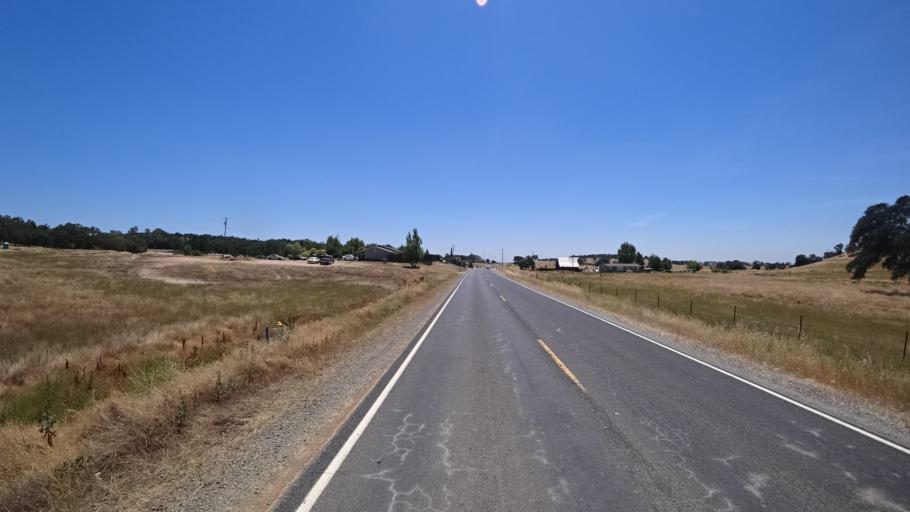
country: US
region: California
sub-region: Calaveras County
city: Rancho Calaveras
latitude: 38.1134
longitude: -120.8794
